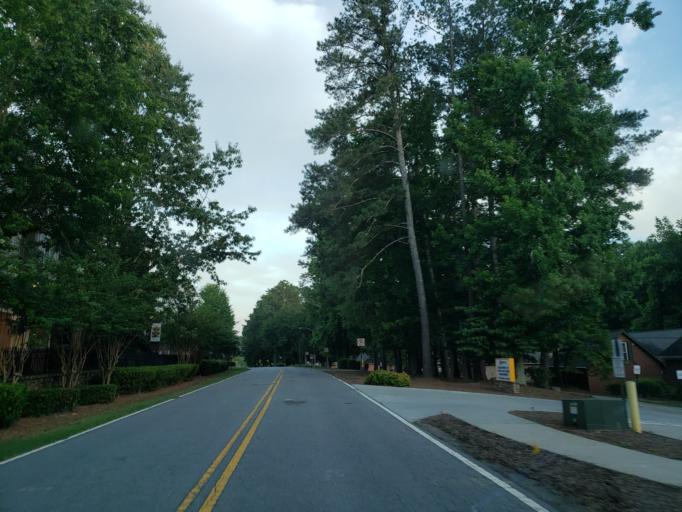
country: US
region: Georgia
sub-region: Cobb County
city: Kennesaw
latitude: 34.0332
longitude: -84.5855
